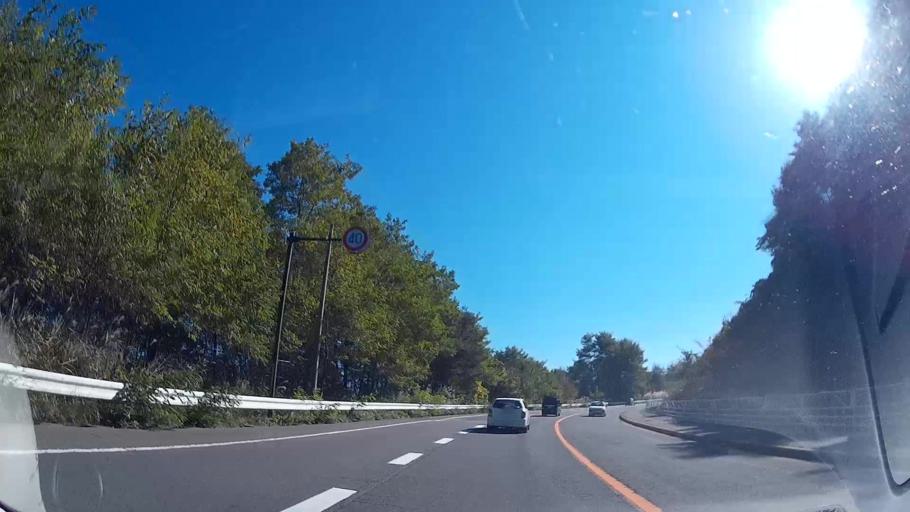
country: JP
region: Nagano
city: Okaya
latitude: 36.0813
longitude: 138.0377
